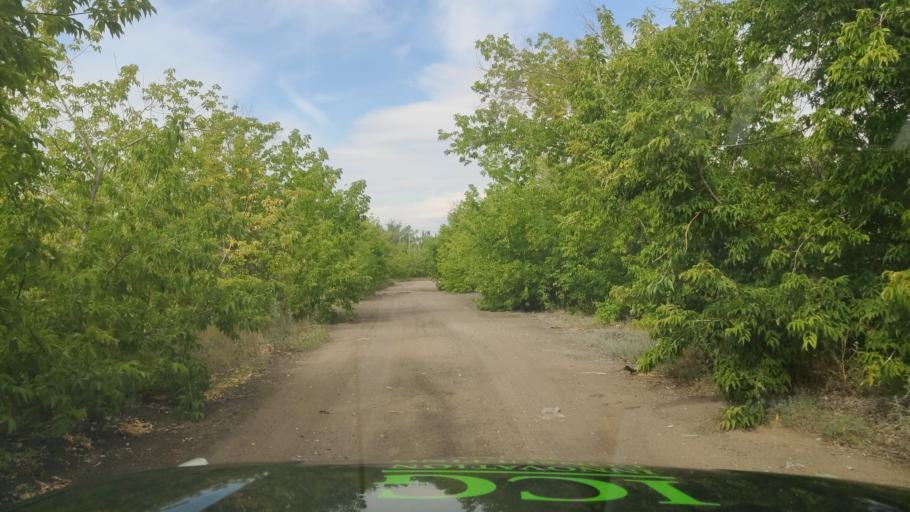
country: KZ
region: Pavlodar
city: Leninskiy
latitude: 52.4965
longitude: 76.8227
